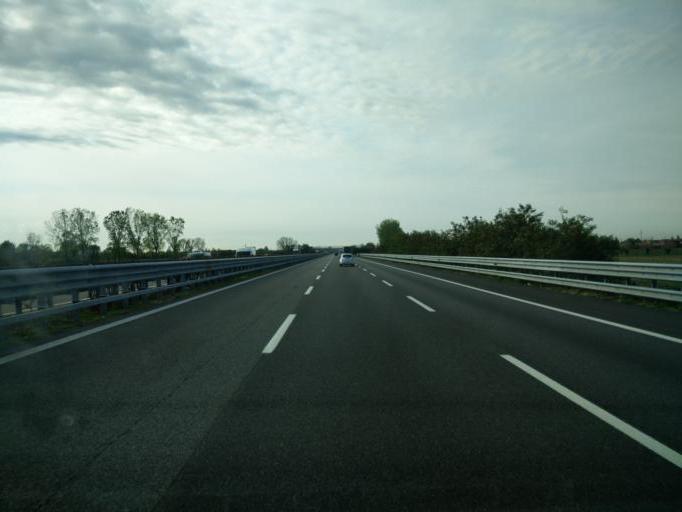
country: IT
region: Lombardy
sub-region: Provincia di Brescia
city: Bagnolo Mella
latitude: 45.4389
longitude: 10.2066
